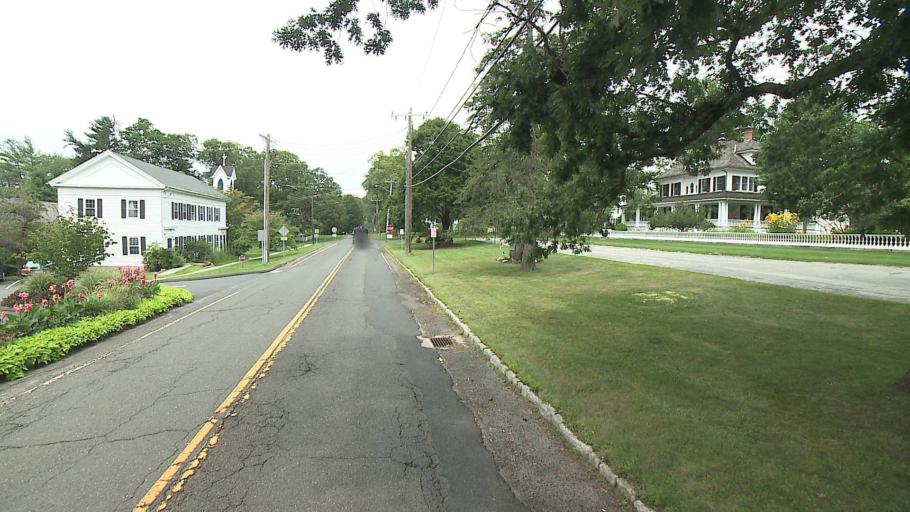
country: US
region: Connecticut
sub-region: Litchfield County
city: New Milford
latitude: 41.5343
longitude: -73.3660
